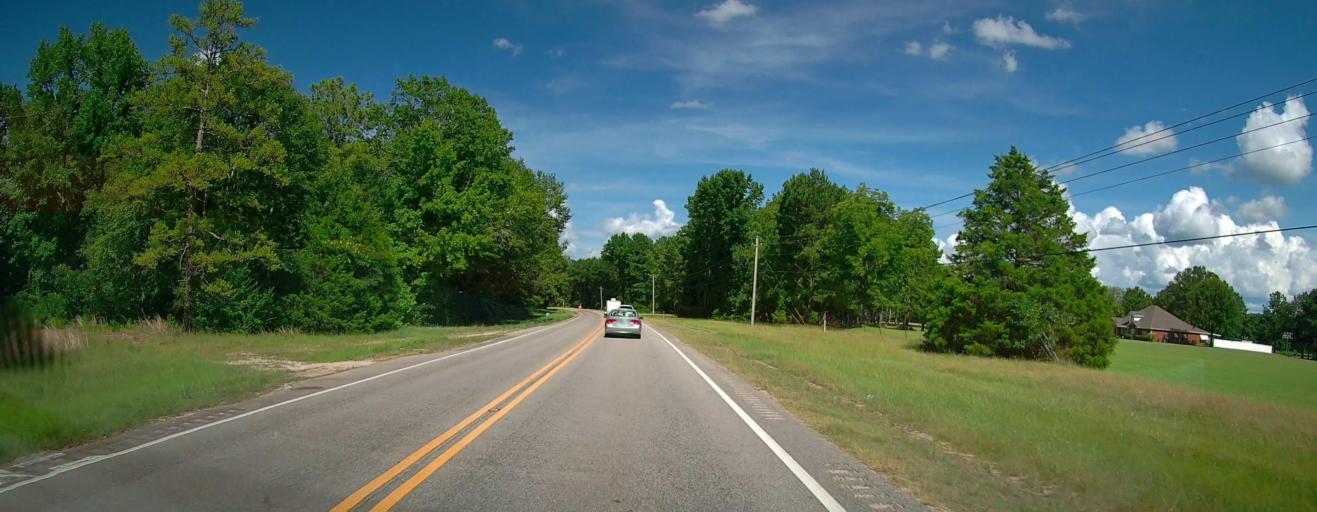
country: US
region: Alabama
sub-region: Macon County
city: Tuskegee
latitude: 32.3748
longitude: -85.8416
